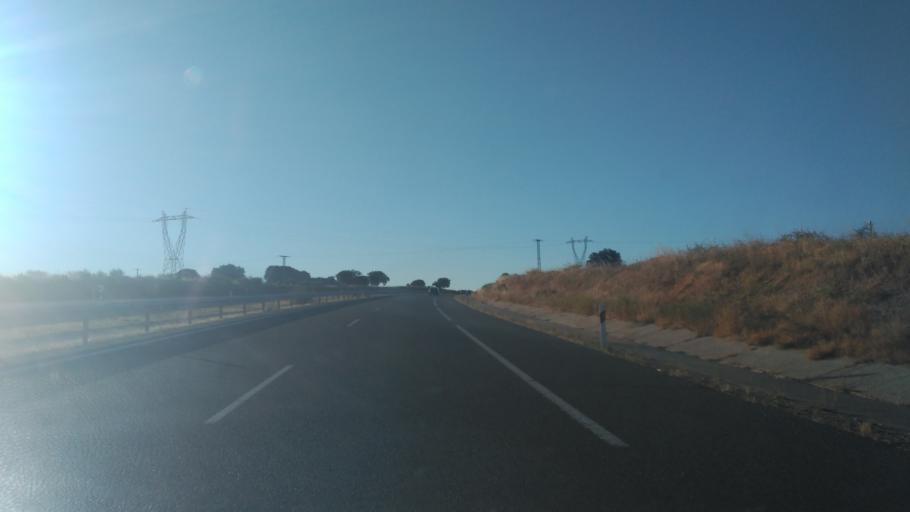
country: ES
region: Castille and Leon
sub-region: Provincia de Salamanca
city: Belena
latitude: 40.7206
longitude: -5.6288
